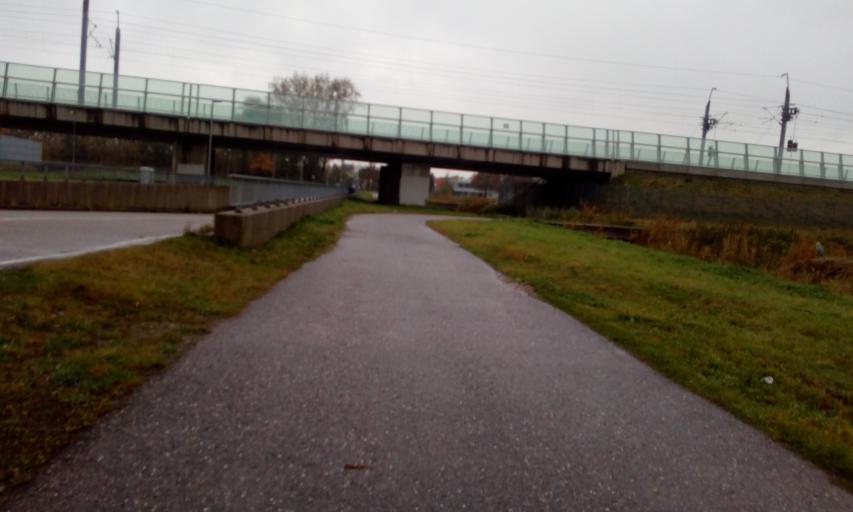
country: NL
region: South Holland
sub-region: Gemeente Lansingerland
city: Berkel en Rodenrijs
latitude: 51.9789
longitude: 4.4722
